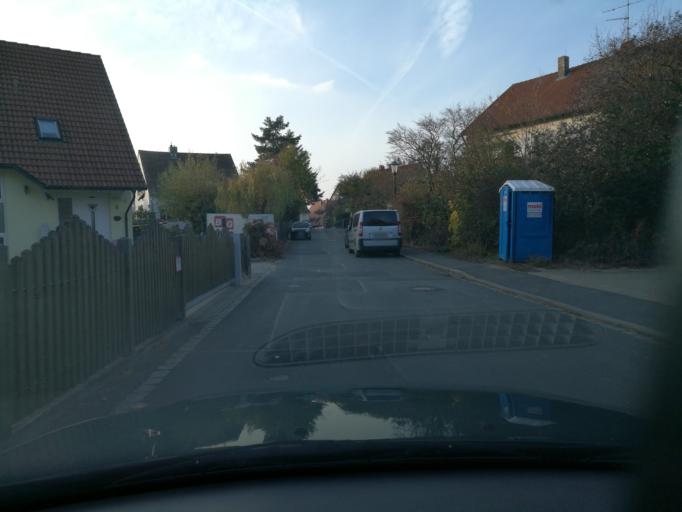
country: DE
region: Bavaria
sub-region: Regierungsbezirk Mittelfranken
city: Furth
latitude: 49.5105
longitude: 10.9769
